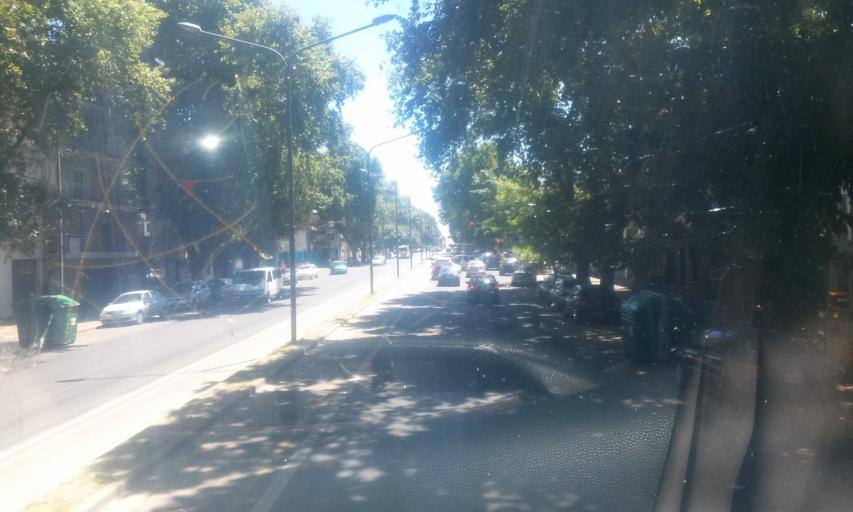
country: AR
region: Santa Fe
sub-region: Departamento de Rosario
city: Rosario
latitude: -32.9426
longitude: -60.6800
